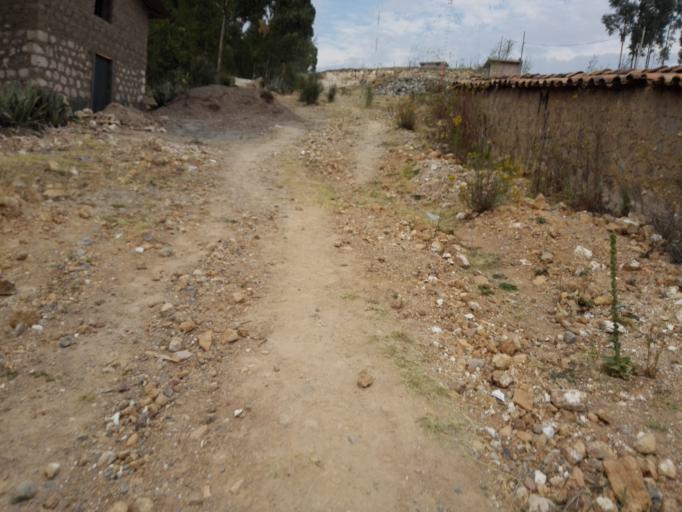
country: PE
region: Ayacucho
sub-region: Provincia de Huamanga
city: Ayacucho
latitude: -13.1503
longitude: -74.2370
